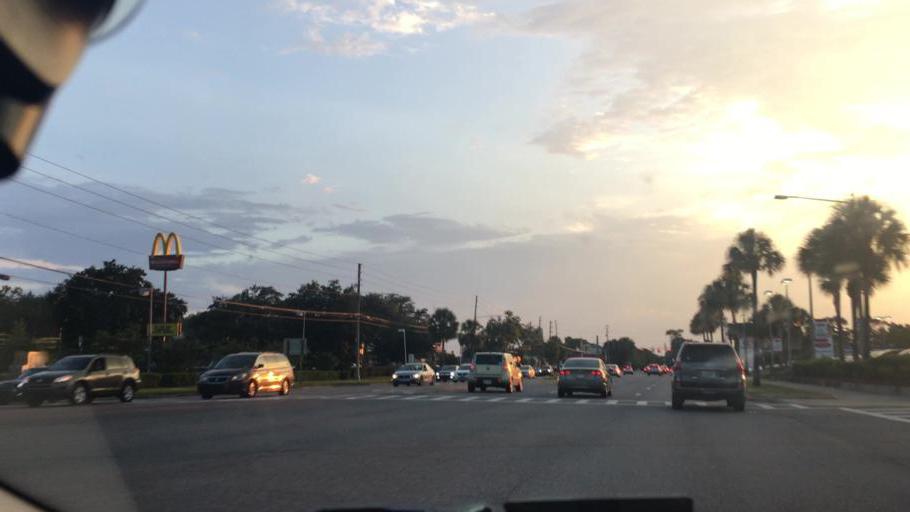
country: US
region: Florida
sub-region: Seminole County
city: Goldenrod
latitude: 28.5973
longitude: -81.3044
